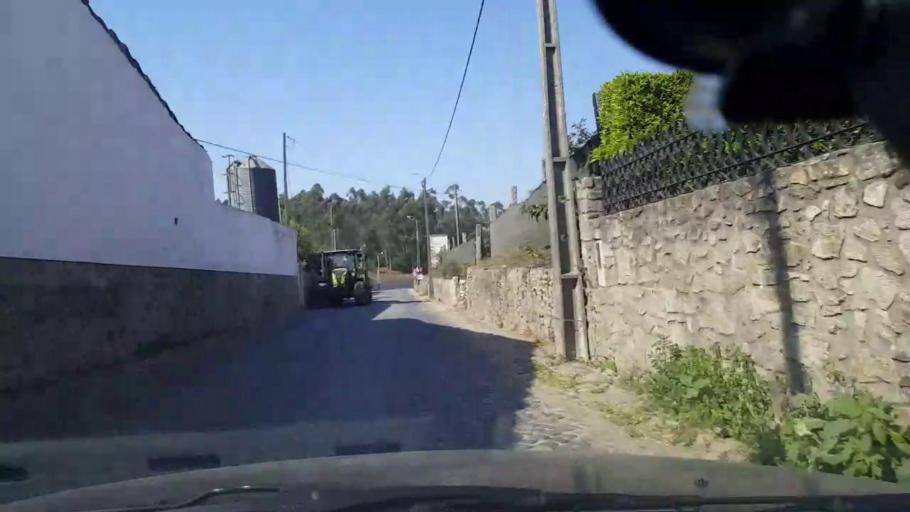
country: PT
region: Porto
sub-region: Vila do Conde
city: Arvore
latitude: 41.3856
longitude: -8.6860
